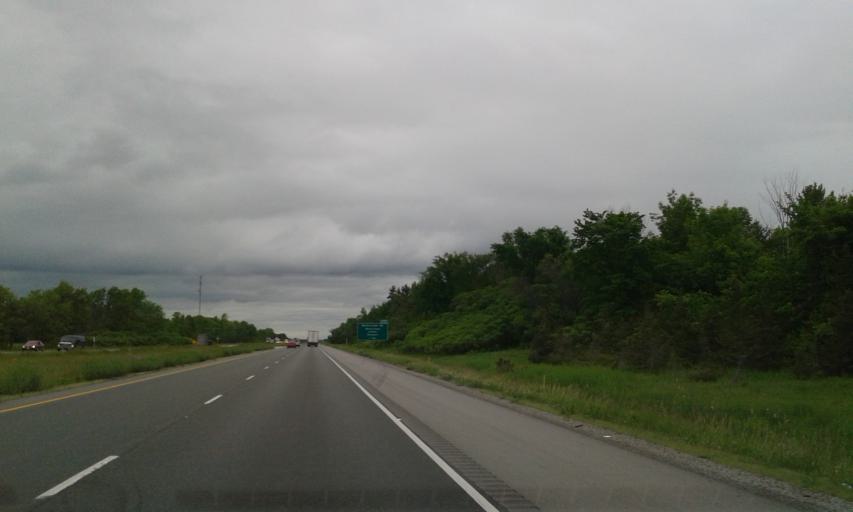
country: US
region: New York
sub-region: Jefferson County
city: Alexandria Bay
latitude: 44.4620
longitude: -75.8794
